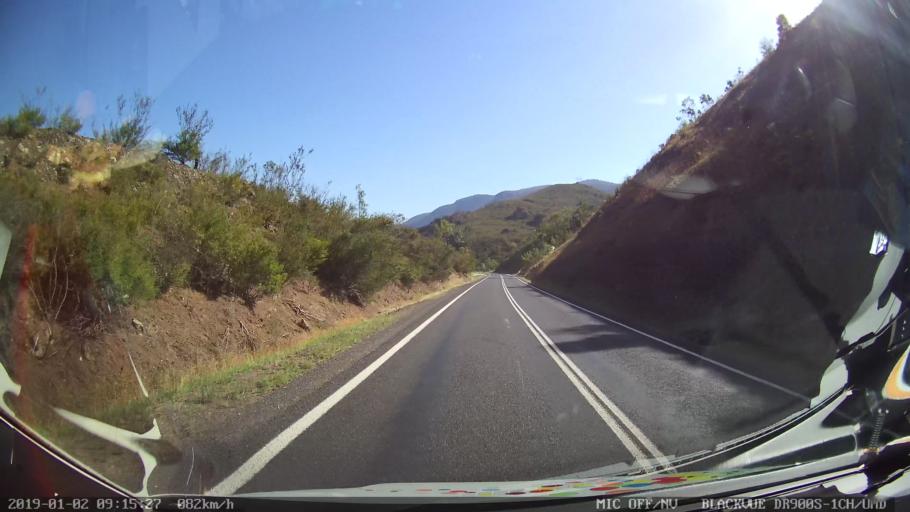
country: AU
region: New South Wales
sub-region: Tumut Shire
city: Tumut
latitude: -35.4648
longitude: 148.2793
